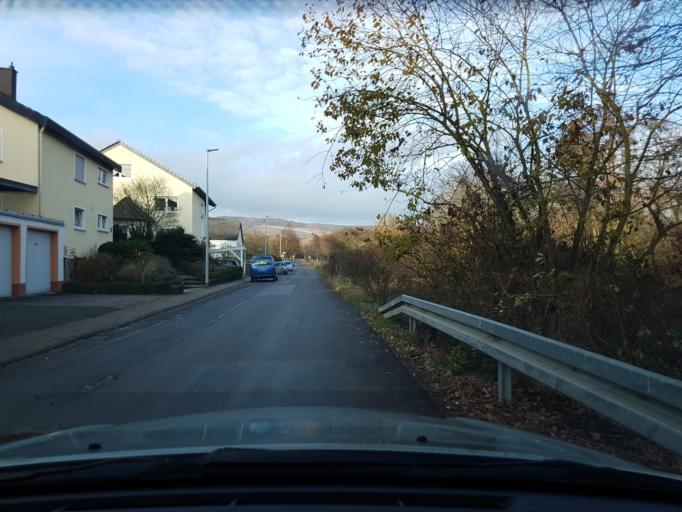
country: DE
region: Hesse
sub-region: Regierungsbezirk Darmstadt
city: Kiedrich
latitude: 50.0205
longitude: 8.0514
